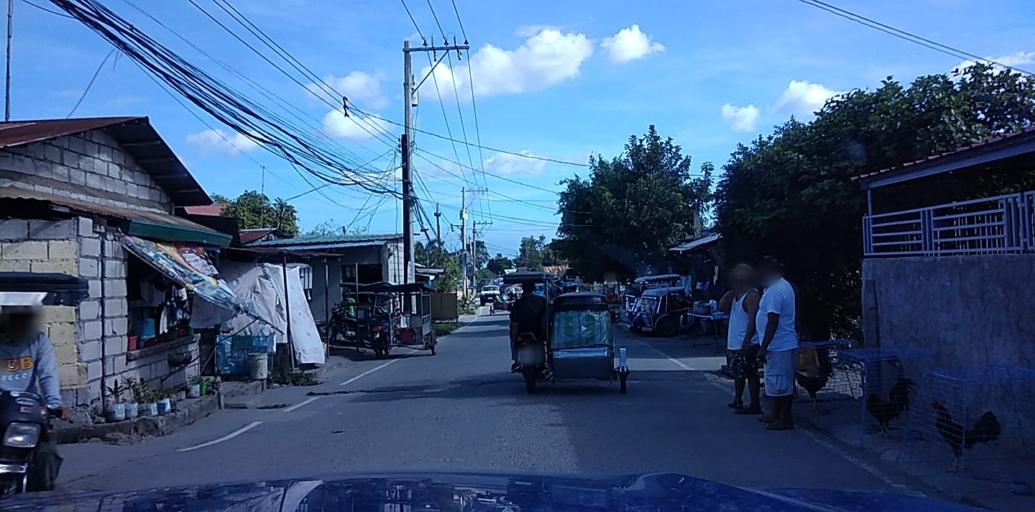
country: PH
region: Central Luzon
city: Santol
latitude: 15.1472
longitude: 120.5478
